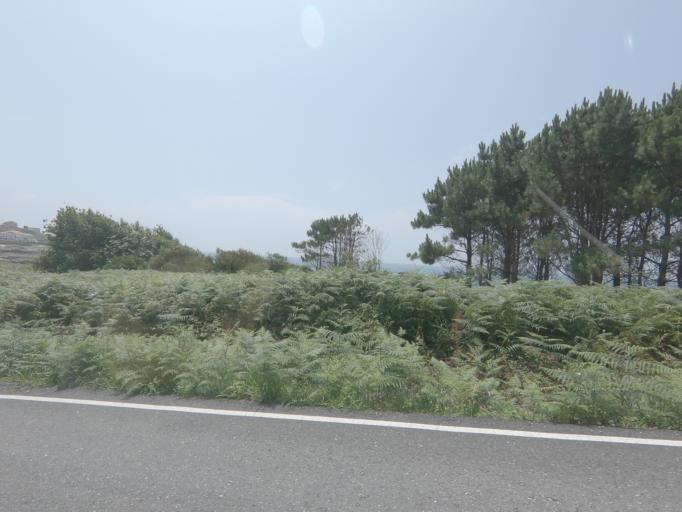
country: ES
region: Galicia
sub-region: Provincia de Pontevedra
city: A Guarda
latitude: 41.9113
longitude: -8.8771
